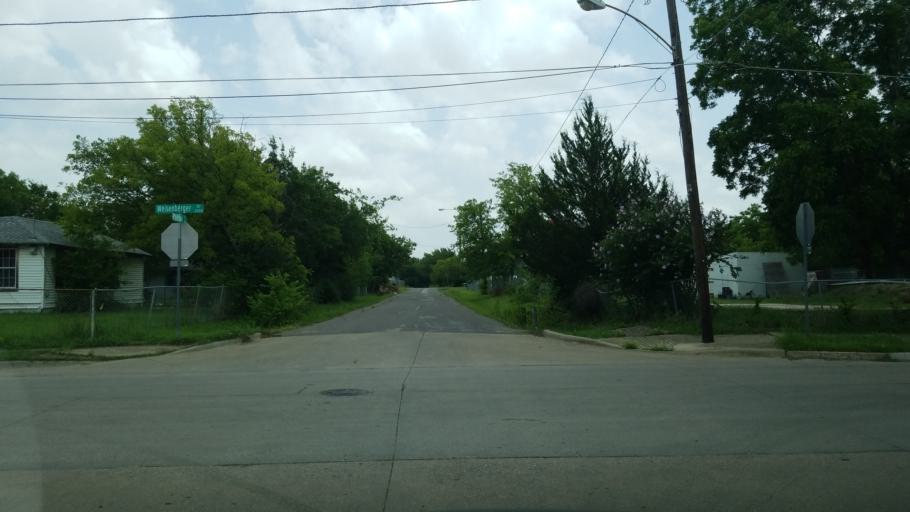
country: US
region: Texas
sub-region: Dallas County
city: Cockrell Hill
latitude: 32.7809
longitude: -96.8972
